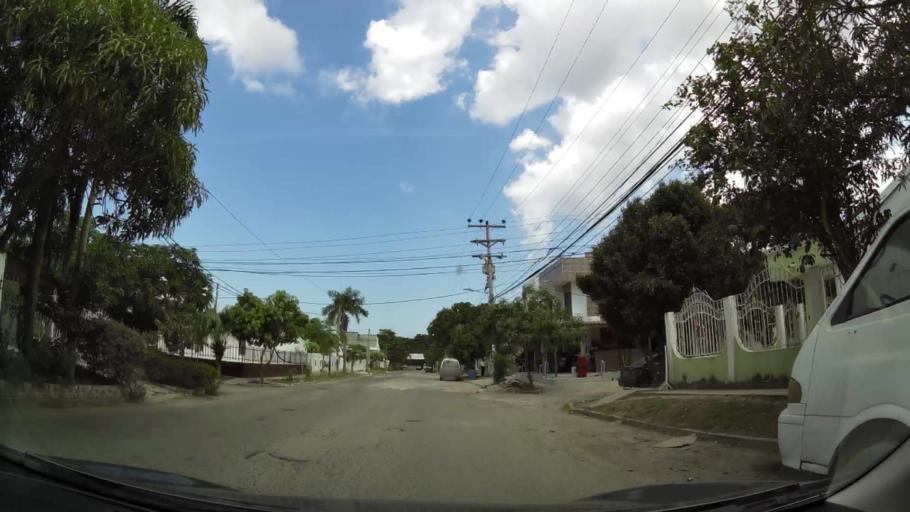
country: CO
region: Bolivar
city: Cartagena
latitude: 10.3729
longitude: -75.4598
